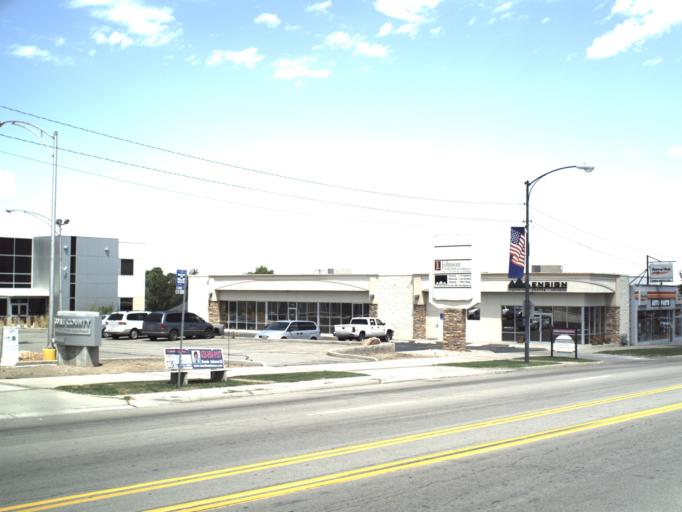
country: US
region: Utah
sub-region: Tooele County
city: Tooele
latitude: 40.5301
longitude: -112.2985
